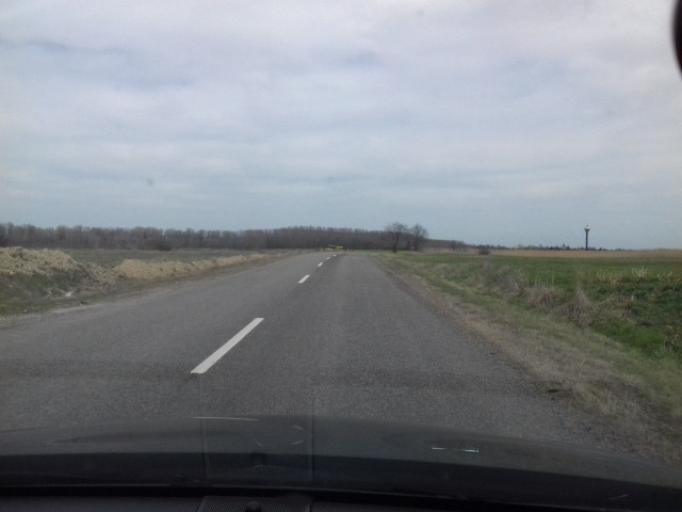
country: HU
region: Bacs-Kiskun
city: Tiszakecske
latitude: 46.8955
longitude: 20.1335
